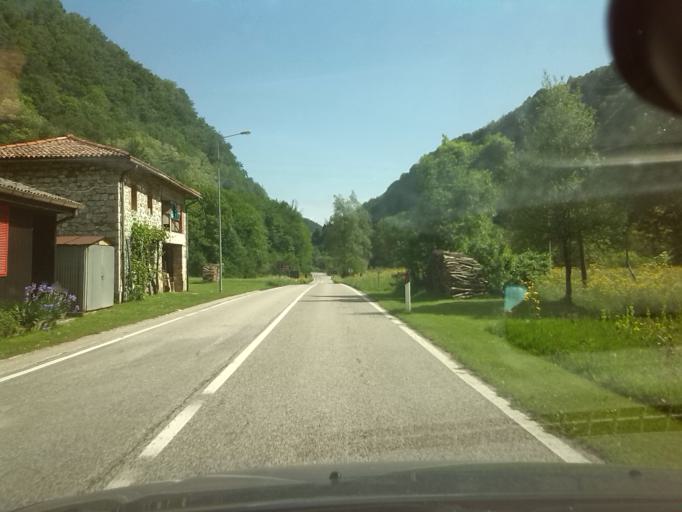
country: IT
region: Friuli Venezia Giulia
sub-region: Provincia di Udine
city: Pulfero
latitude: 46.1797
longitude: 13.4780
